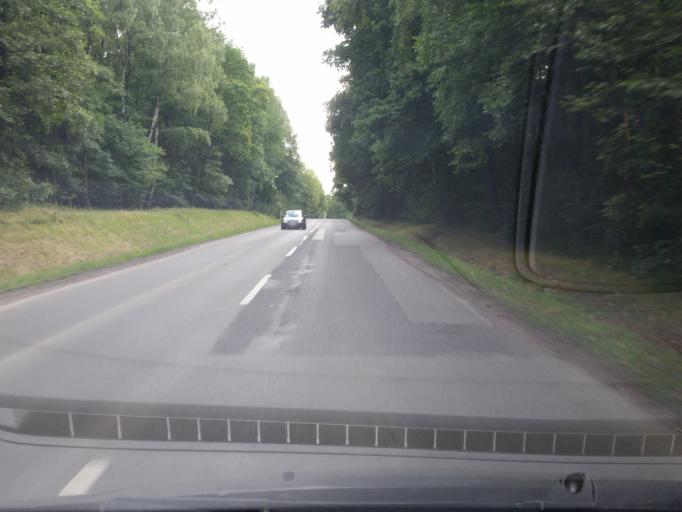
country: PL
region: Silesian Voivodeship
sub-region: Powiat pszczynski
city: Pawlowice
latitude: 49.9582
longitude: 18.6899
